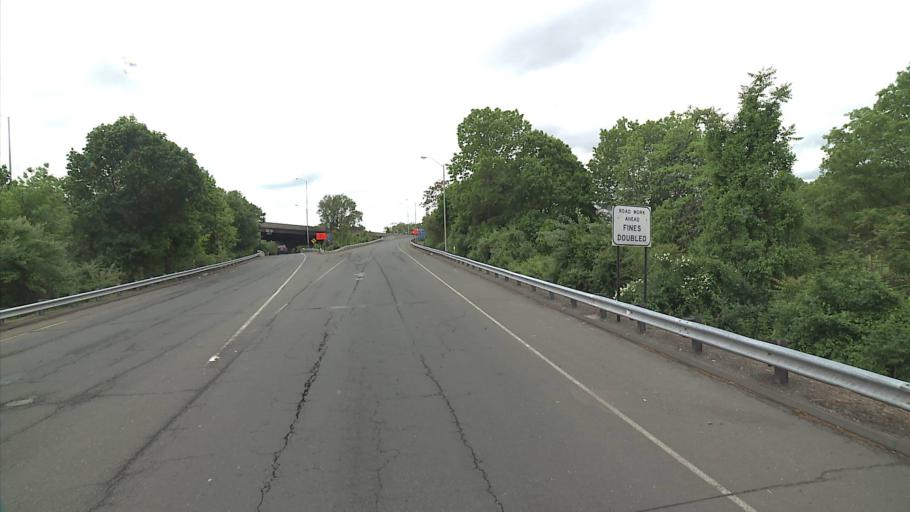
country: US
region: Connecticut
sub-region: New Haven County
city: New Haven
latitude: 41.3186
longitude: -72.9045
